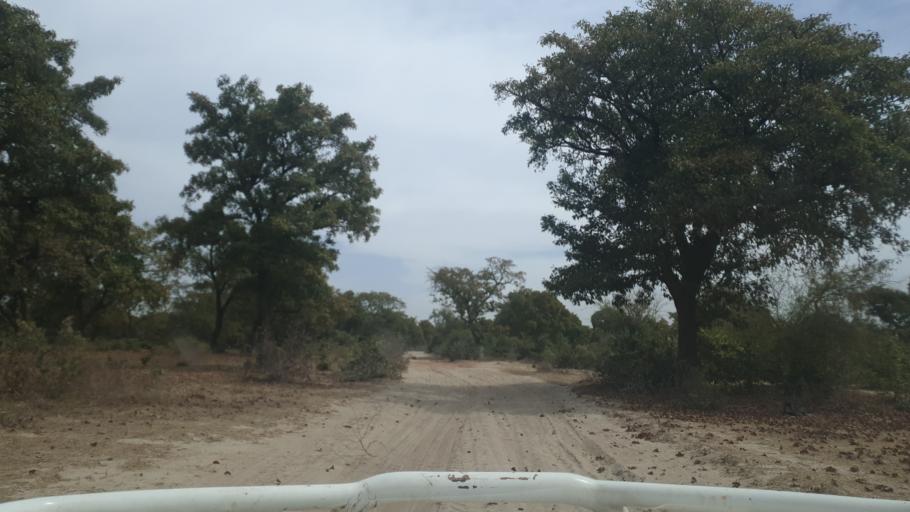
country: ML
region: Sikasso
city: Yorosso
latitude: 12.2370
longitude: -4.7406
